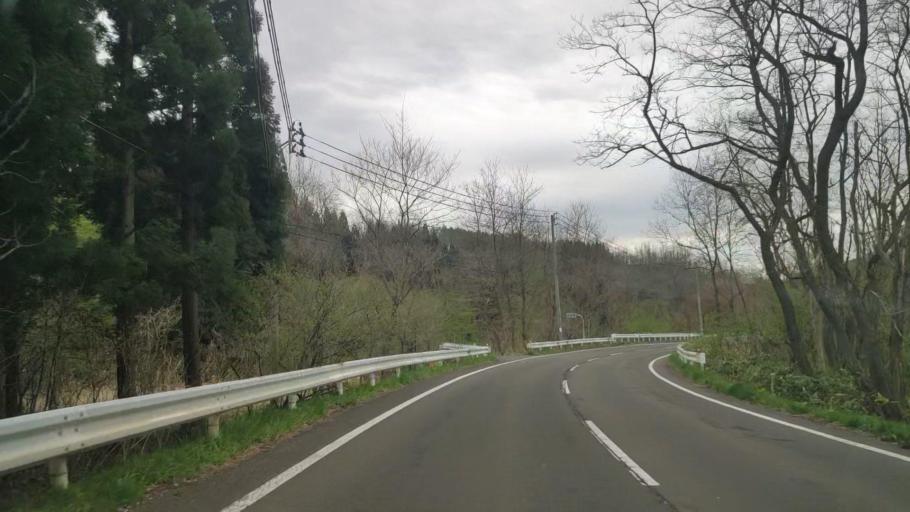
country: JP
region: Akita
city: Hanawa
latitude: 40.3466
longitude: 140.7742
